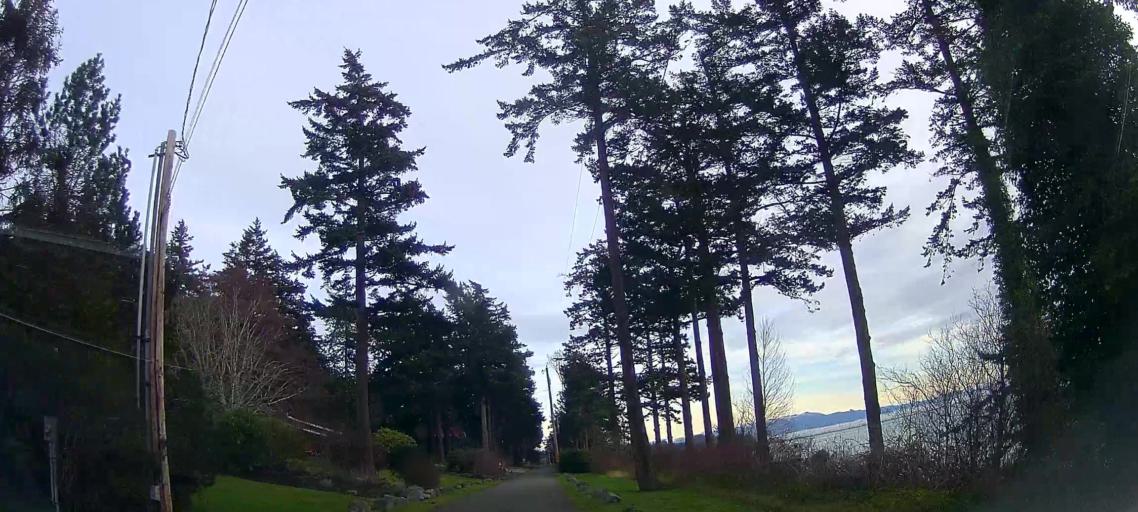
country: US
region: Washington
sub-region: Skagit County
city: Anacortes
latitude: 48.5760
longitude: -122.5502
